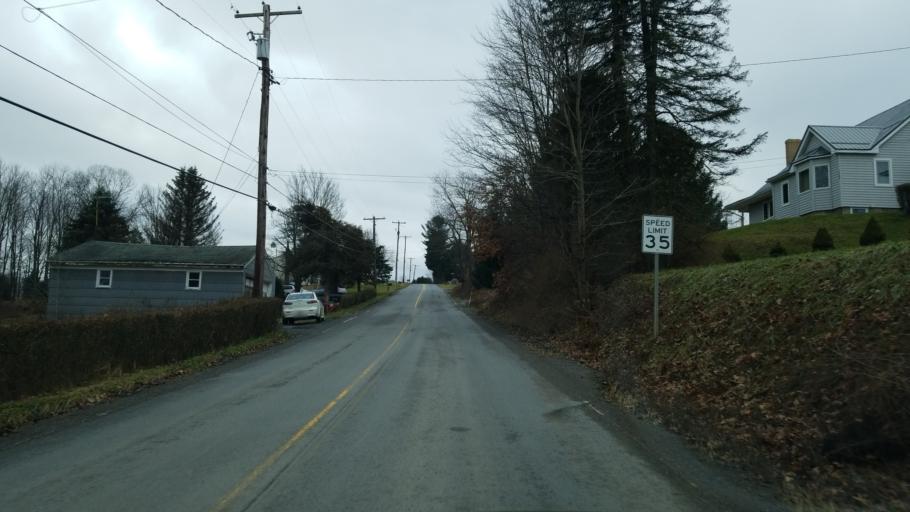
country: US
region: Pennsylvania
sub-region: Clearfield County
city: Clearfield
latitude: 41.0342
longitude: -78.4687
